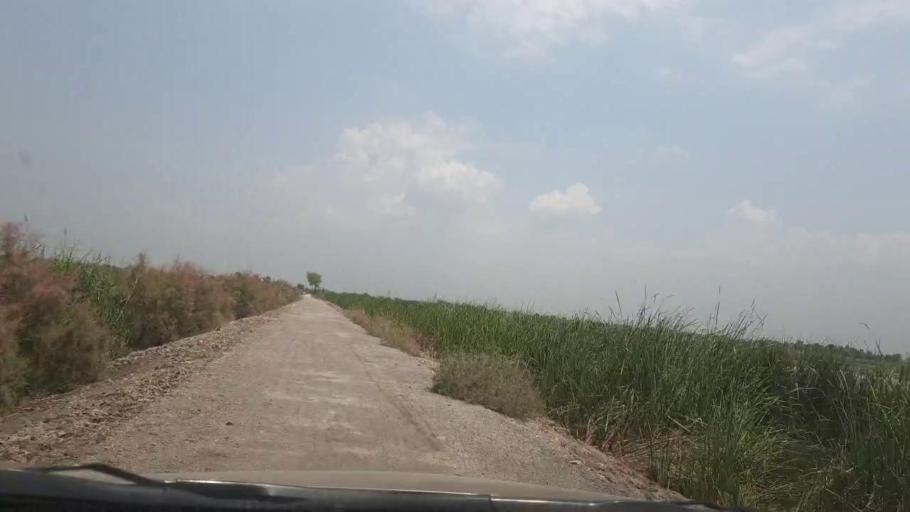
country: PK
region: Sindh
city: Naudero
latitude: 27.7224
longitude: 68.3247
